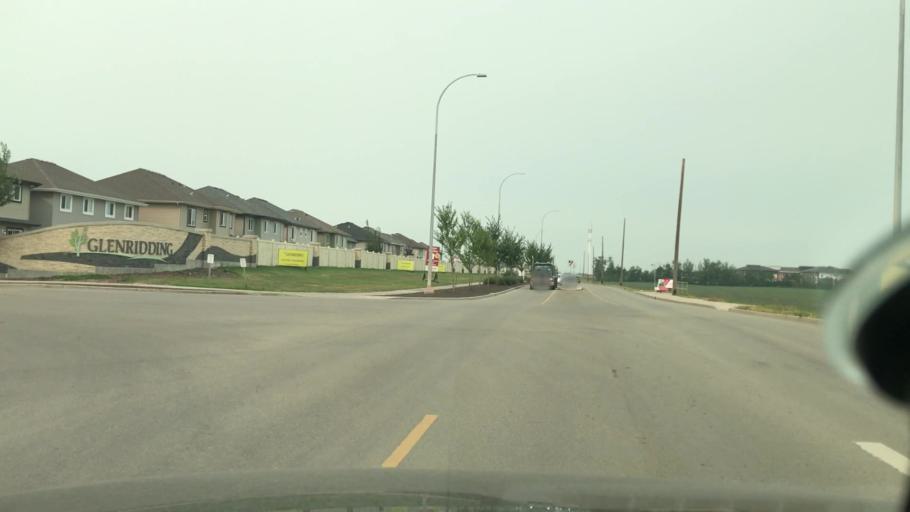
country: CA
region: Alberta
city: Devon
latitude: 53.4249
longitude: -113.5966
